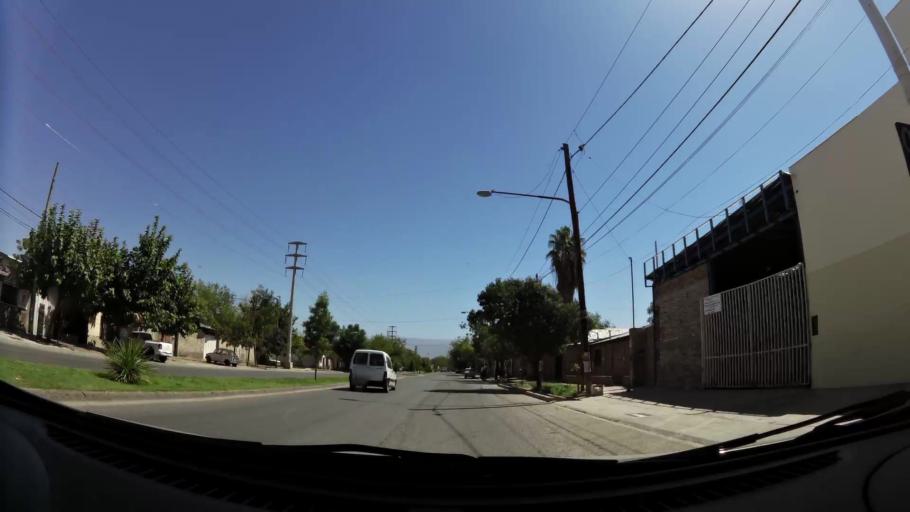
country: AR
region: Mendoza
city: Villa Nueva
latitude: -32.8807
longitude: -68.8000
